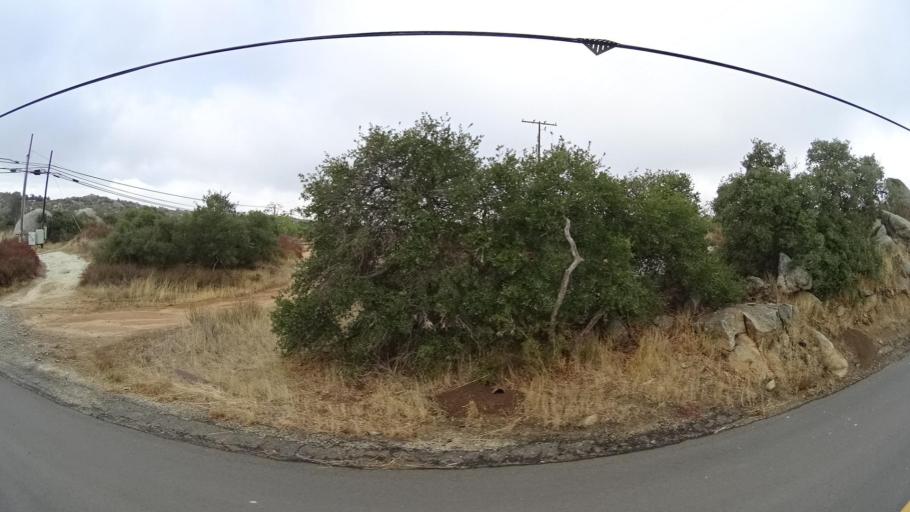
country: MX
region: Baja California
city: Tecate
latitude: 32.6004
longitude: -116.5819
